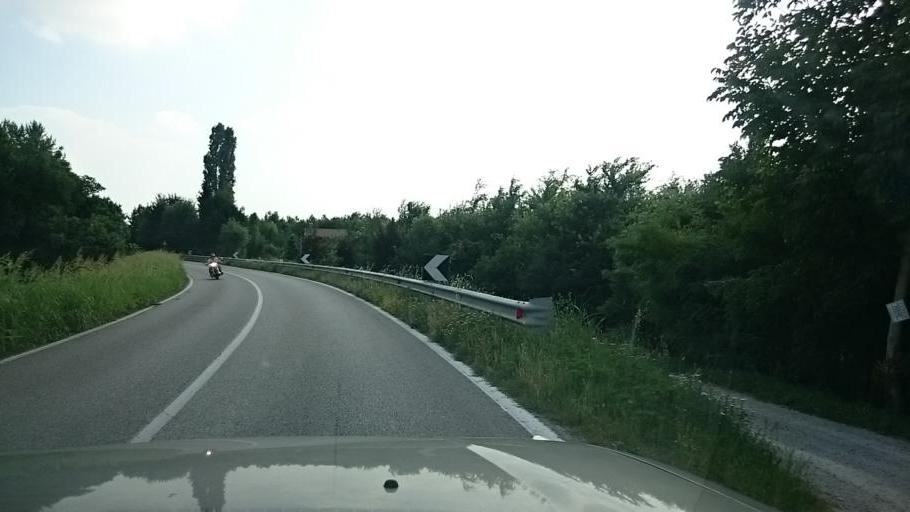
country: IT
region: Veneto
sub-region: Provincia di Padova
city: Santa Maria di Non
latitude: 45.5106
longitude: 11.8622
